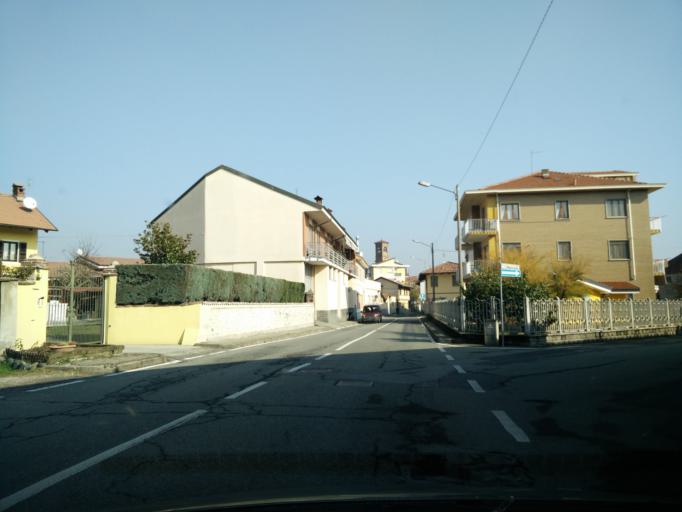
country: IT
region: Piedmont
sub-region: Provincia di Torino
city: Leini
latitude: 45.1835
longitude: 7.7105
